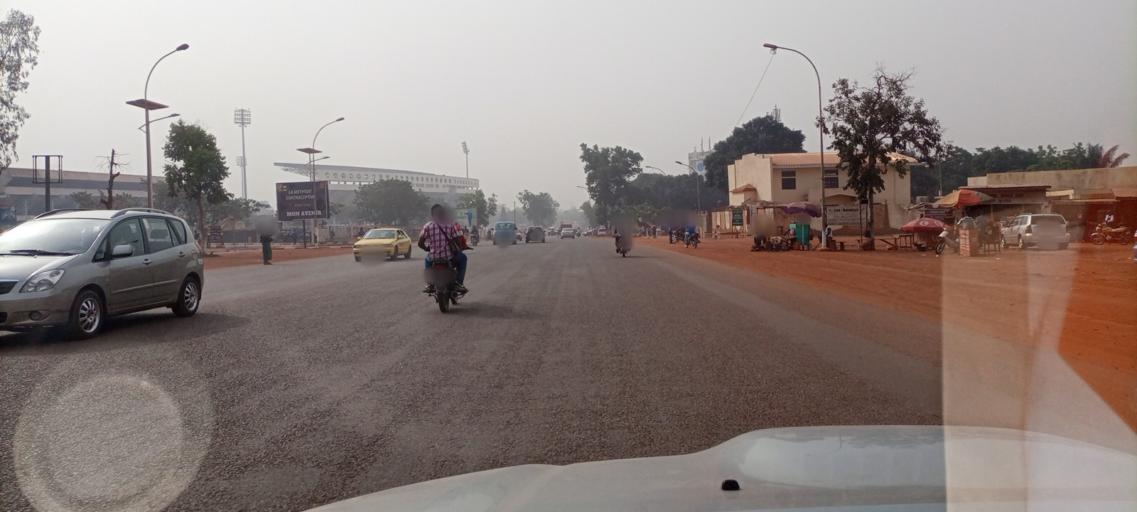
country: CF
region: Bangui
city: Bangui
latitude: 4.3772
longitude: 18.5617
